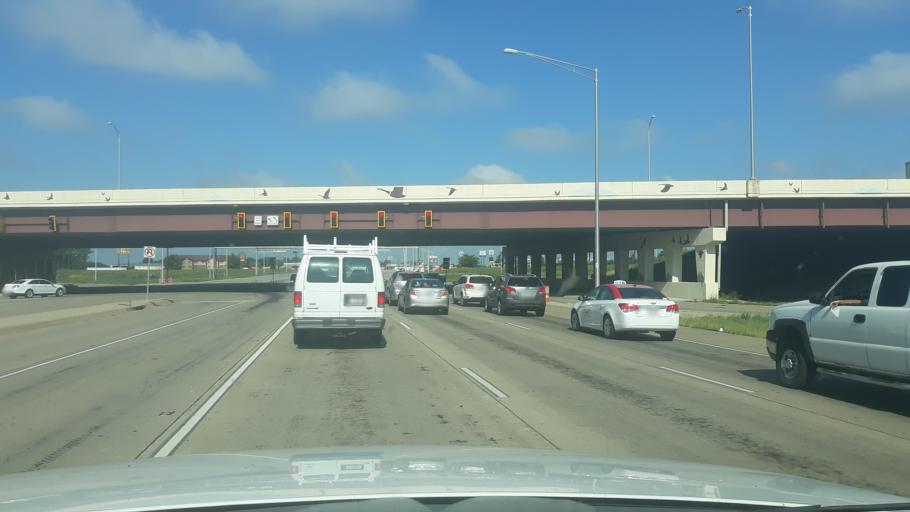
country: US
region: Illinois
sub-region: Williamson County
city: Marion
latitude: 37.7407
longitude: -88.9570
